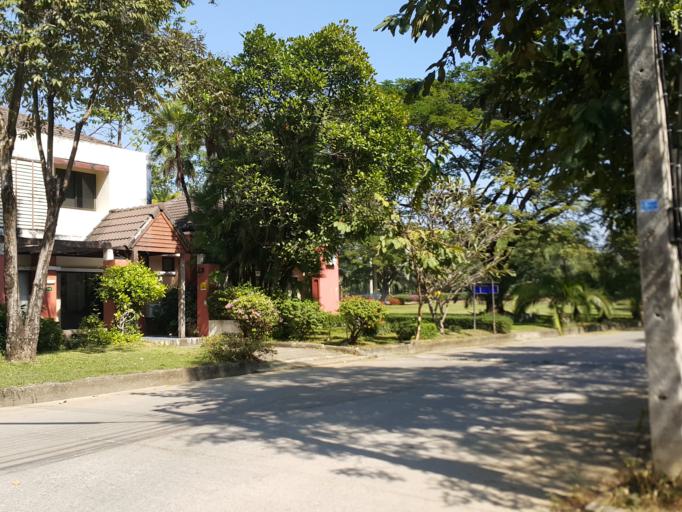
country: TH
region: Chiang Mai
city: Chiang Mai
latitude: 18.8278
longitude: 99.0054
